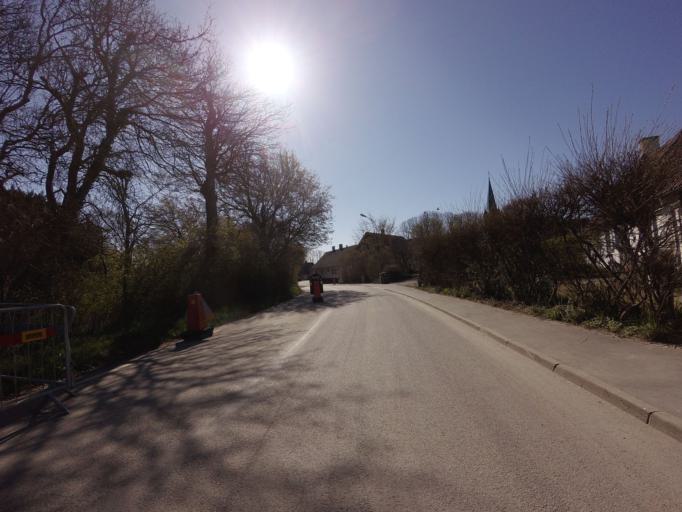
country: SE
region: Skane
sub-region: Malmo
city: Oxie
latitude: 55.4700
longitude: 13.1351
